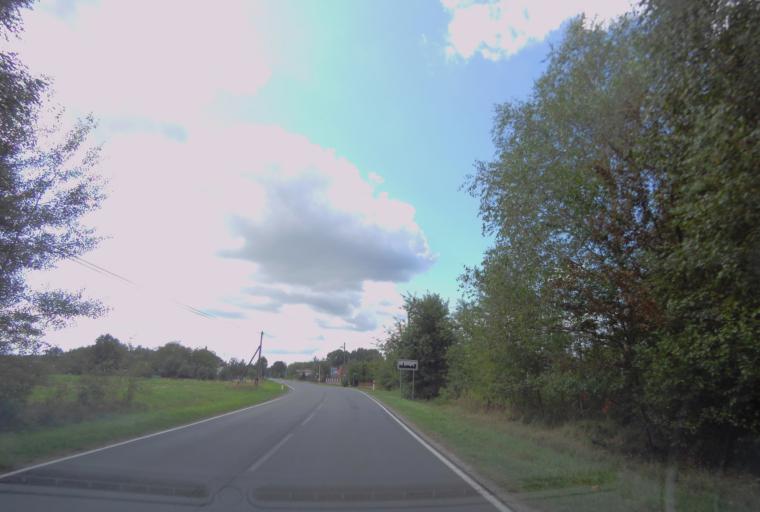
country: PL
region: Subcarpathian Voivodeship
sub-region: Powiat kolbuszowski
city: Majdan Krolewski
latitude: 50.3935
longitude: 21.7674
